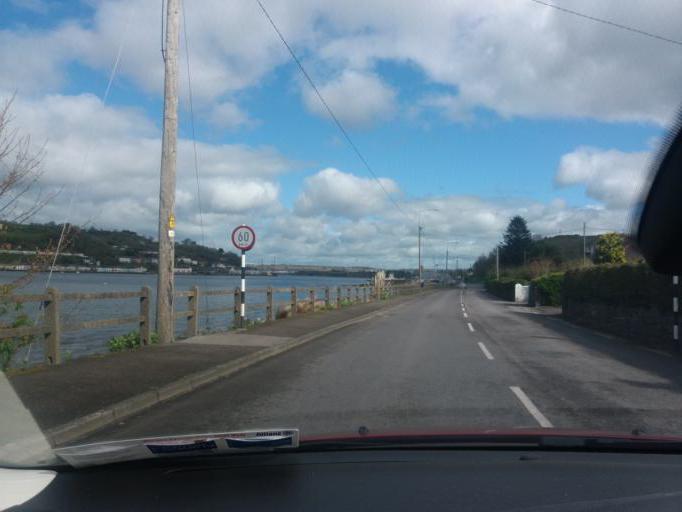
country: IE
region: Munster
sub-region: County Cork
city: Passage West
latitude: 51.8577
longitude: -8.3257
